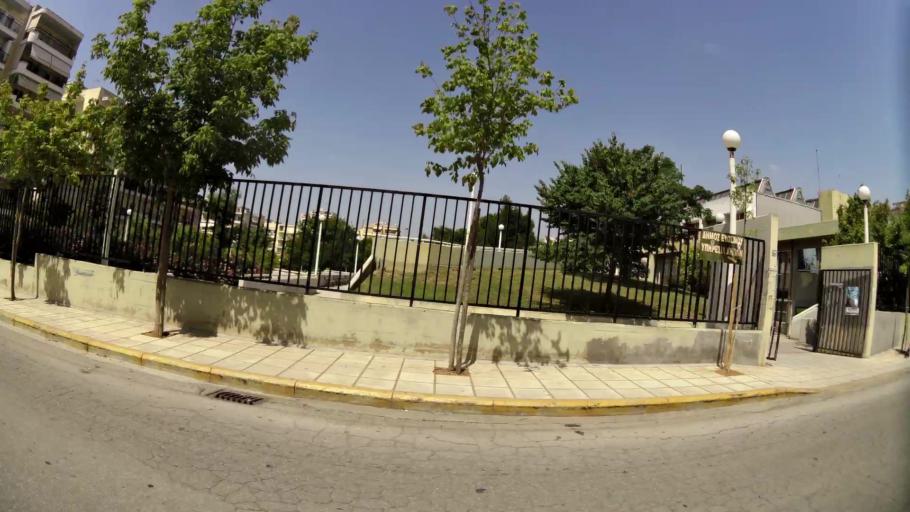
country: GR
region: Central Macedonia
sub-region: Nomos Thessalonikis
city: Evosmos
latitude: 40.6737
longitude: 22.9179
